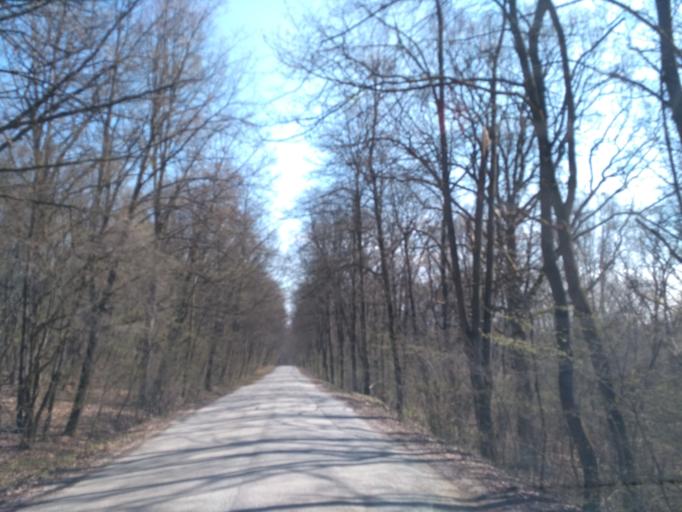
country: SK
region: Kosicky
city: Moldava nad Bodvou
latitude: 48.6489
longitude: 20.9947
